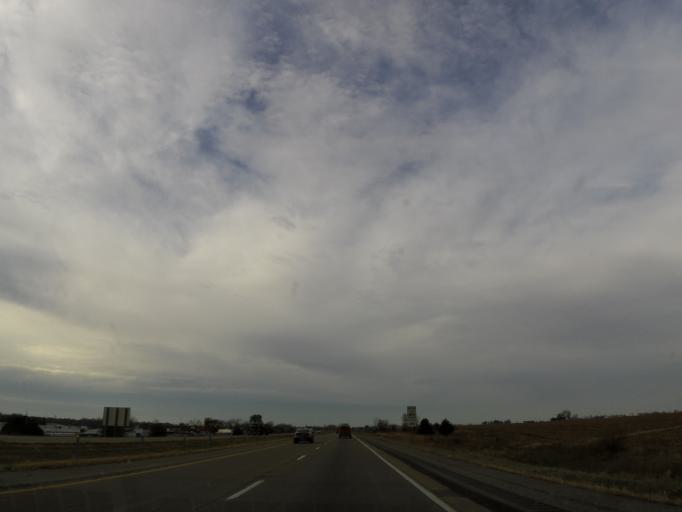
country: US
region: Iowa
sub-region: Scott County
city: Eldridge
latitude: 41.5984
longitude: -90.5831
